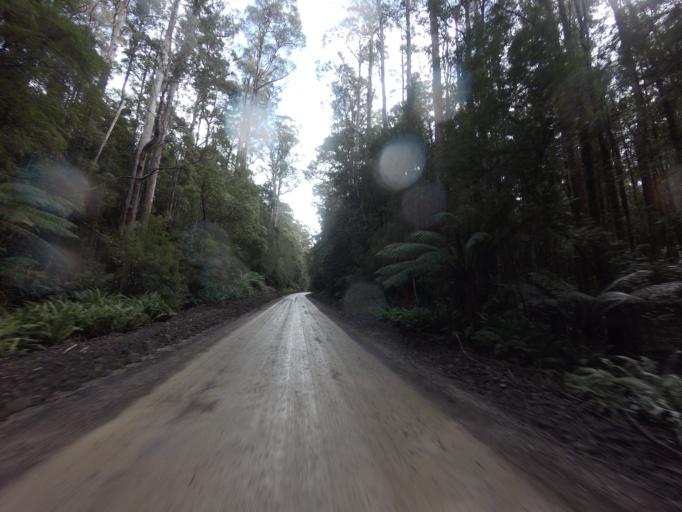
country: AU
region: Tasmania
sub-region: Huon Valley
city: Geeveston
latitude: -43.3869
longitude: 146.8478
